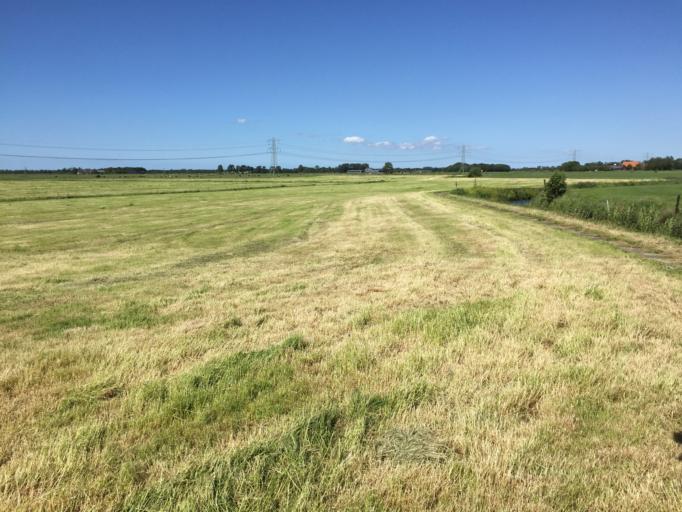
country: NL
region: Friesland
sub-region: Gemeente Boarnsterhim
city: Warten
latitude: 53.1829
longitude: 5.8805
